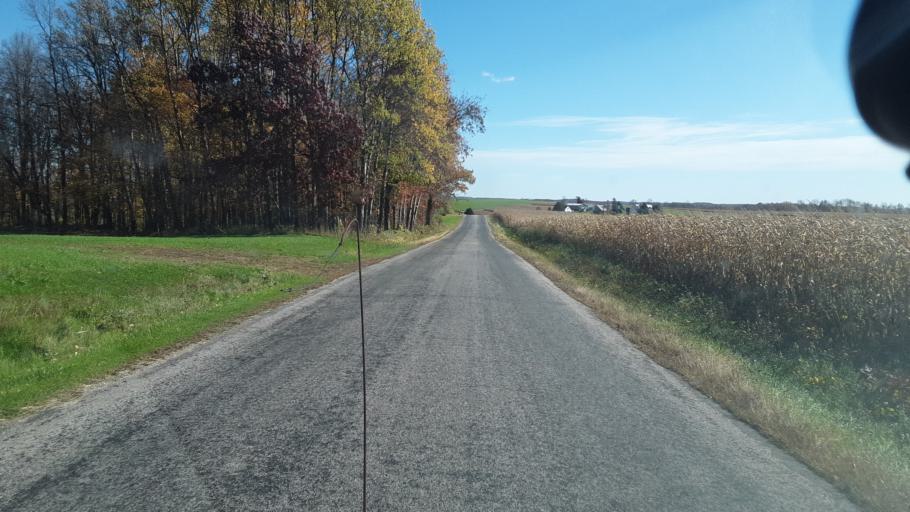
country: US
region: Wisconsin
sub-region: Vernon County
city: Hillsboro
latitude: 43.6901
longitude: -90.4285
